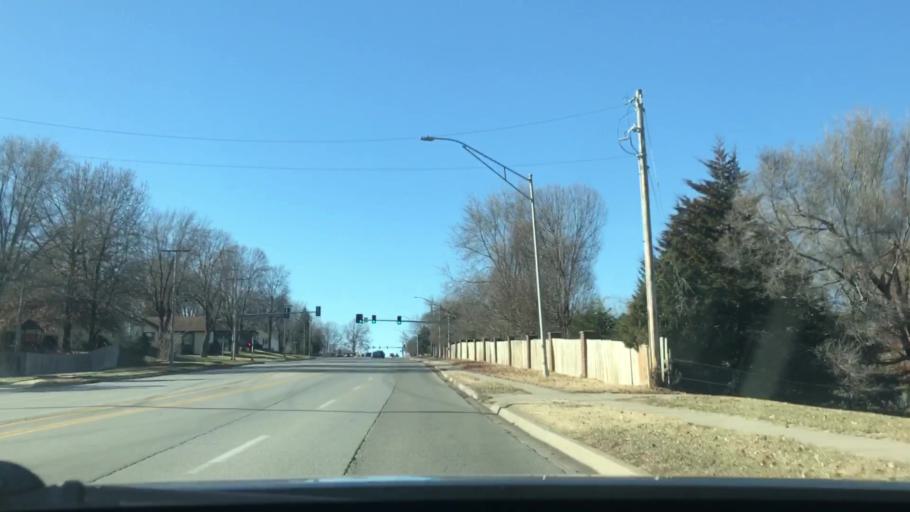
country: US
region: Missouri
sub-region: Jackson County
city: Independence
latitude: 39.0488
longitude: -94.3826
